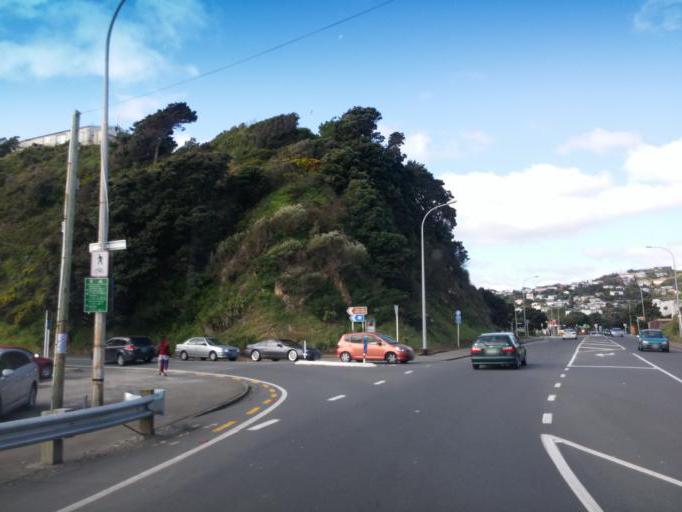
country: NZ
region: Wellington
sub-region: Wellington City
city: Wellington
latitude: -41.3144
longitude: 174.8111
